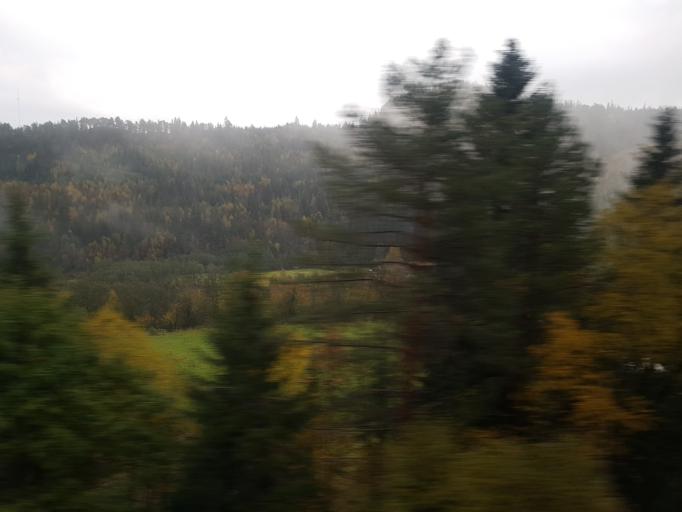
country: NO
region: Sor-Trondelag
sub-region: Midtre Gauldal
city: Storen
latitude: 63.0288
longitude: 10.2657
